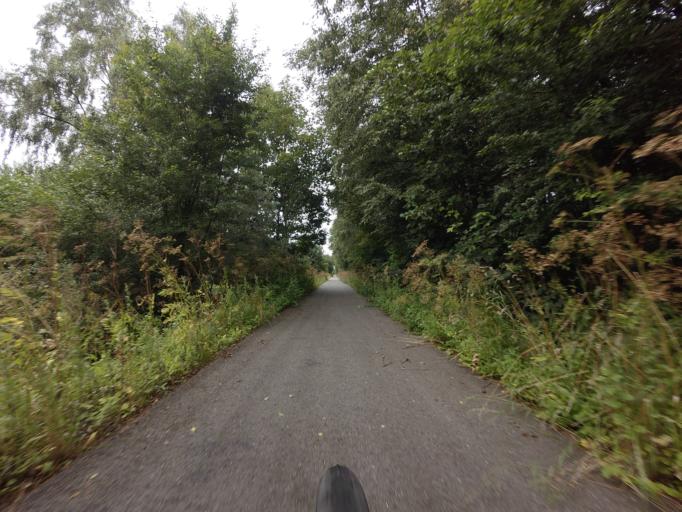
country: DK
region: Central Jutland
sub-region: Syddjurs Kommune
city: Ryomgard
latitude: 56.3859
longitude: 10.4451
